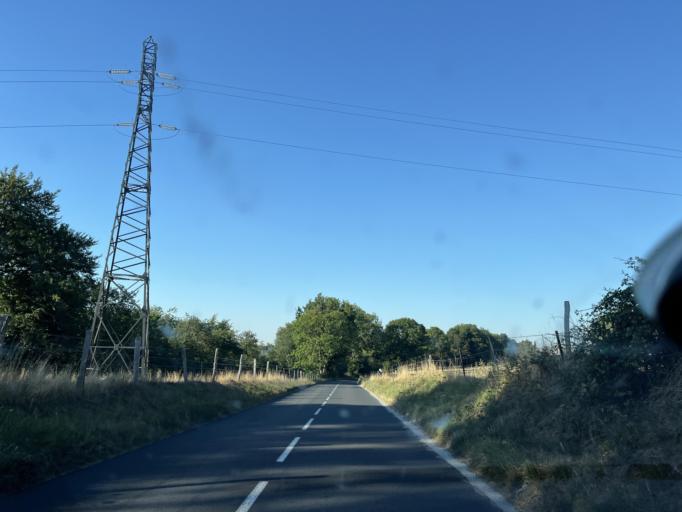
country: FR
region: Haute-Normandie
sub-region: Departement de la Seine-Maritime
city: Lillebonne
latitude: 49.5389
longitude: 0.5513
